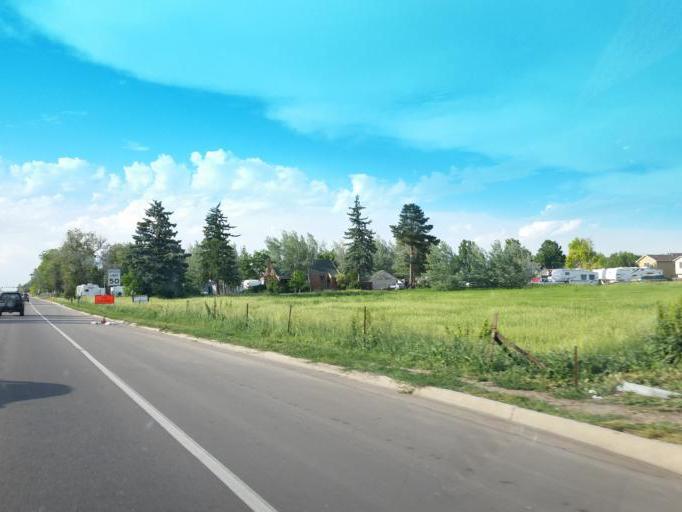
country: US
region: Colorado
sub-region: Larimer County
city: Loveland
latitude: 40.4319
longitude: -105.0774
